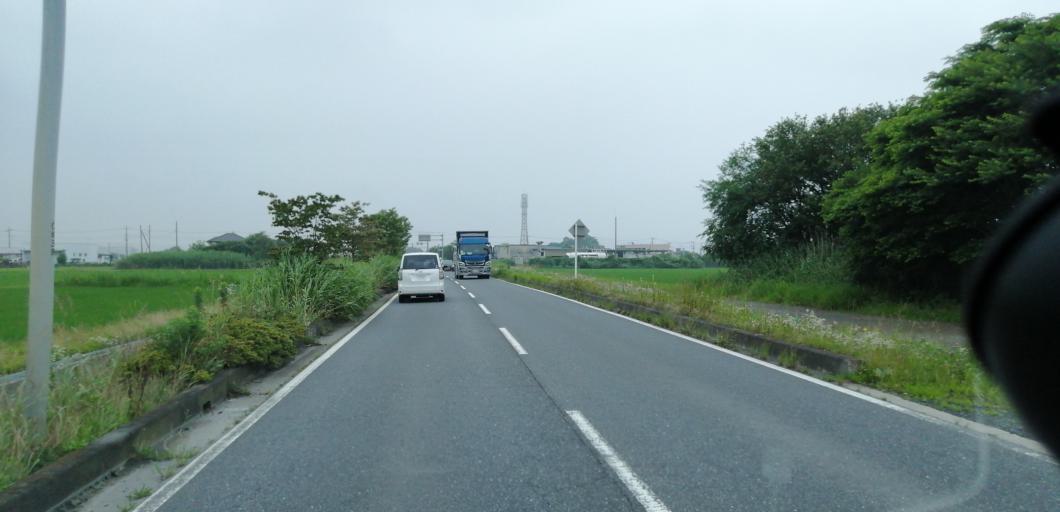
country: JP
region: Saitama
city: Kazo
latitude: 36.1433
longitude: 139.5729
